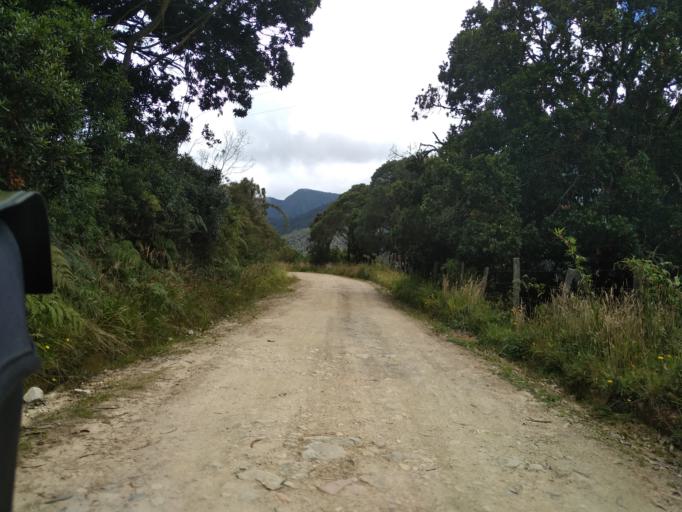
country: CO
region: Boyaca
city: Duitama
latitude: 5.9391
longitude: -73.1180
